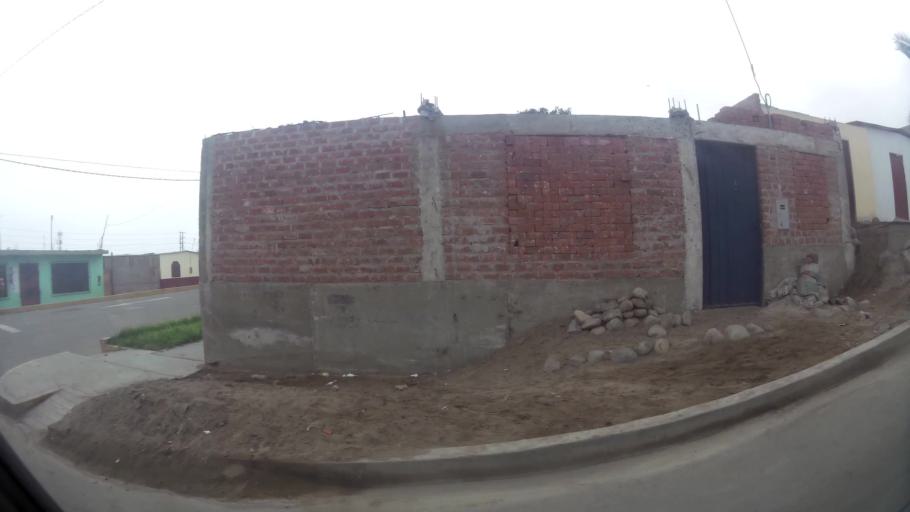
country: PE
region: Lima
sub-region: Provincia de Huaral
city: Chancay
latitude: -11.5951
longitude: -77.2543
